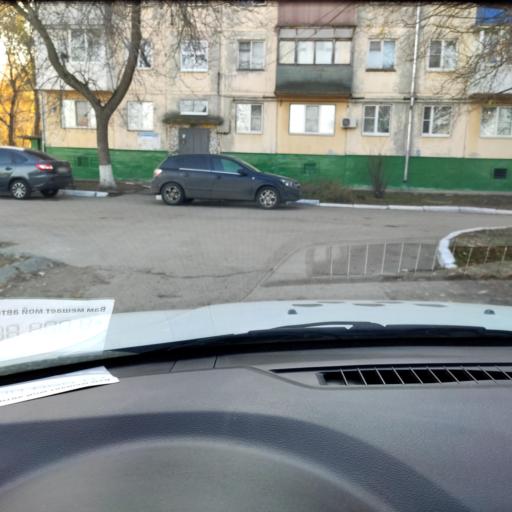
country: RU
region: Samara
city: Tol'yatti
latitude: 53.5331
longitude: 49.4271
